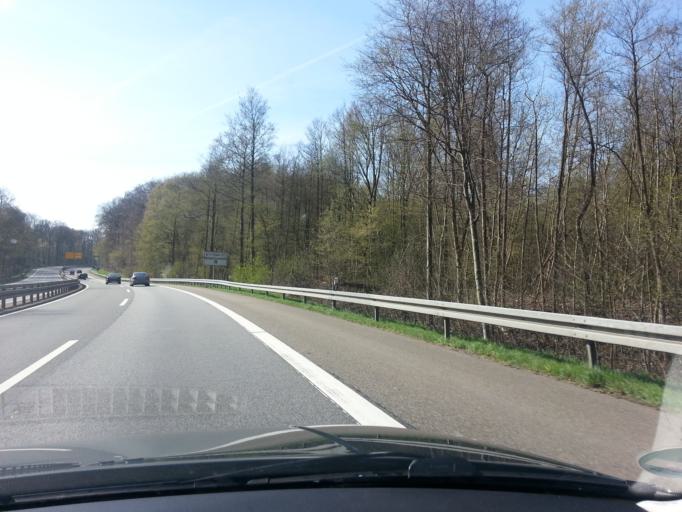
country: DE
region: Saarland
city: Saarbrucken
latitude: 49.2645
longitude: 6.9936
